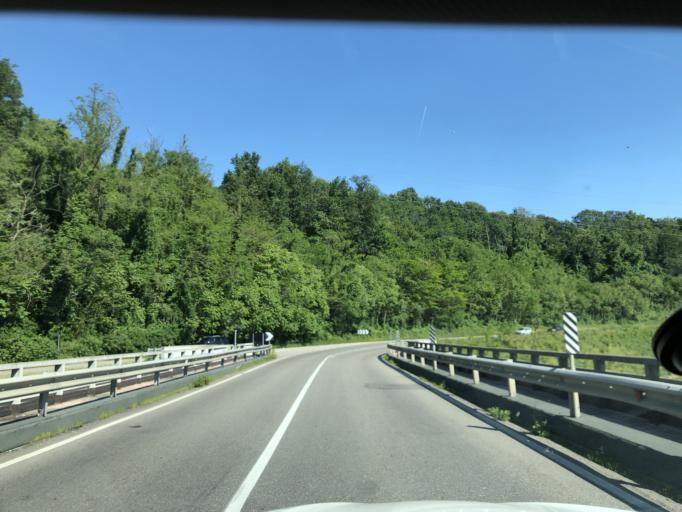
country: IT
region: Lombardy
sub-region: Citta metropolitana di Milano
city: Nosate
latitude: 45.5866
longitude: 8.7066
